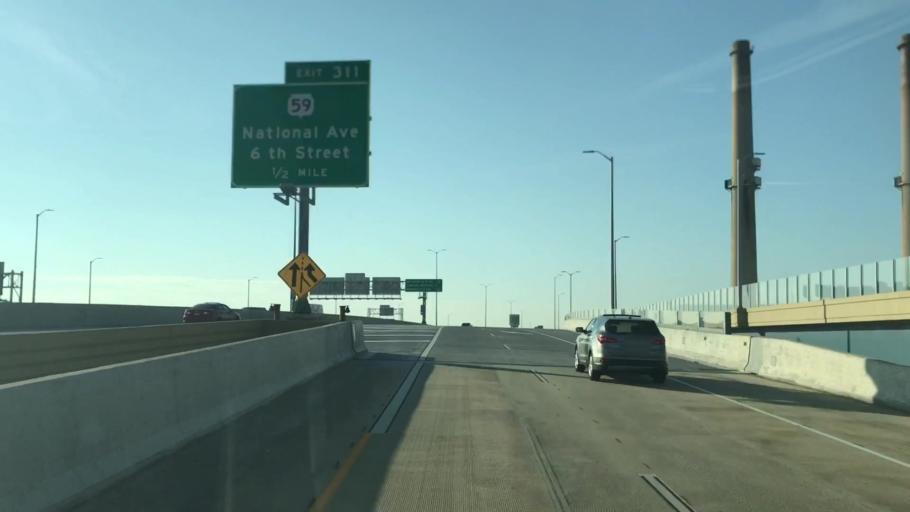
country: US
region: Wisconsin
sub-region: Milwaukee County
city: Milwaukee
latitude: 43.0325
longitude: -87.9230
